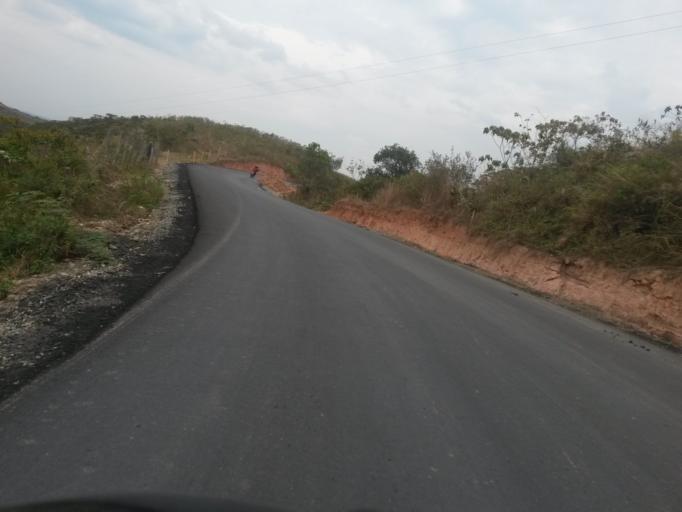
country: CO
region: Cauca
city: Buenos Aires
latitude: 3.0565
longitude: -76.6290
